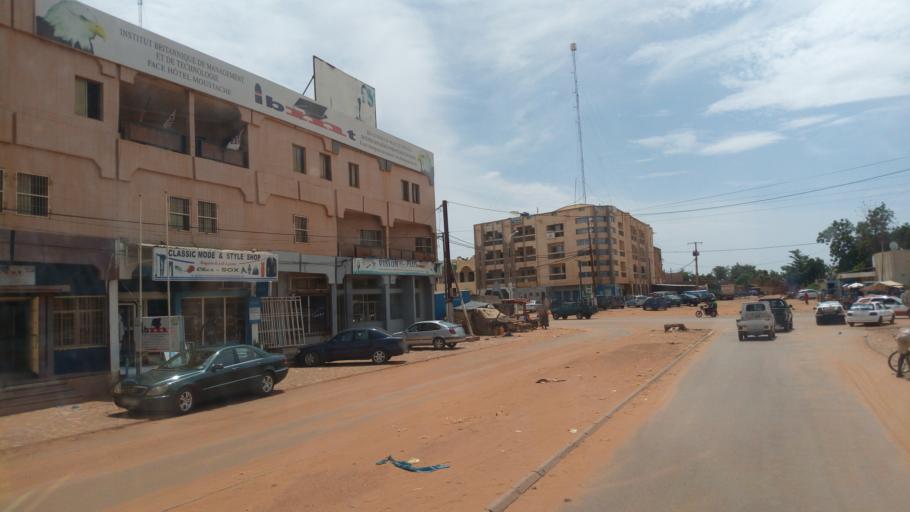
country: NE
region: Niamey
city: Niamey
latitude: 13.5167
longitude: 2.1288
